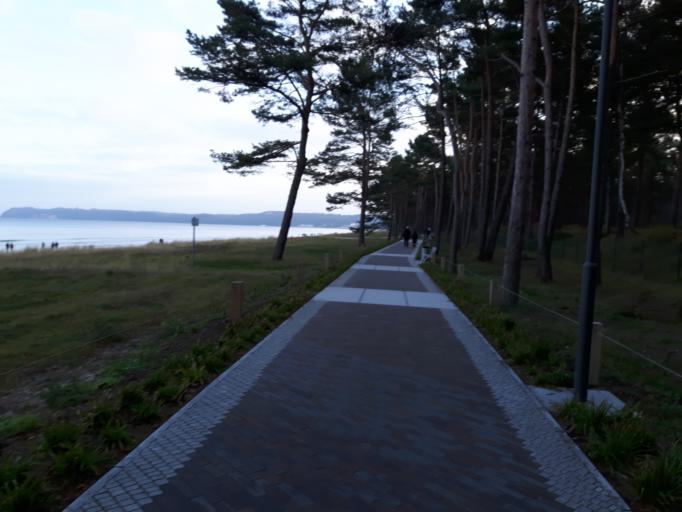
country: DE
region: Mecklenburg-Vorpommern
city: Ostseebad Binz
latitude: 54.4203
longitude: 13.5913
